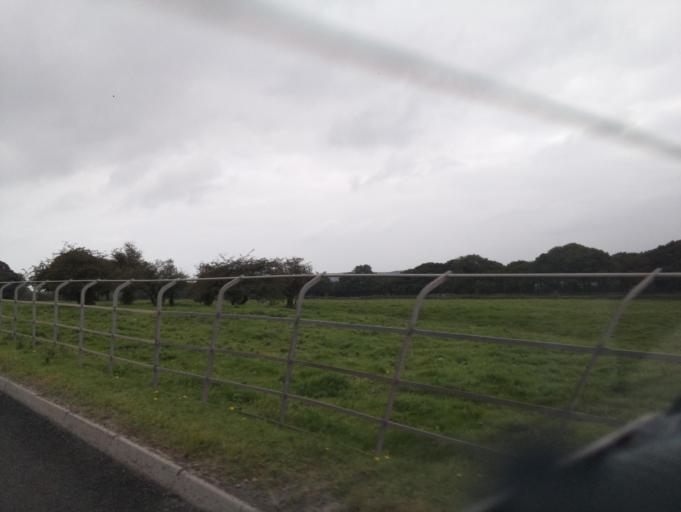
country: GB
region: England
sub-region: Staffordshire
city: Cheadle
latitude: 53.0309
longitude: -1.9220
